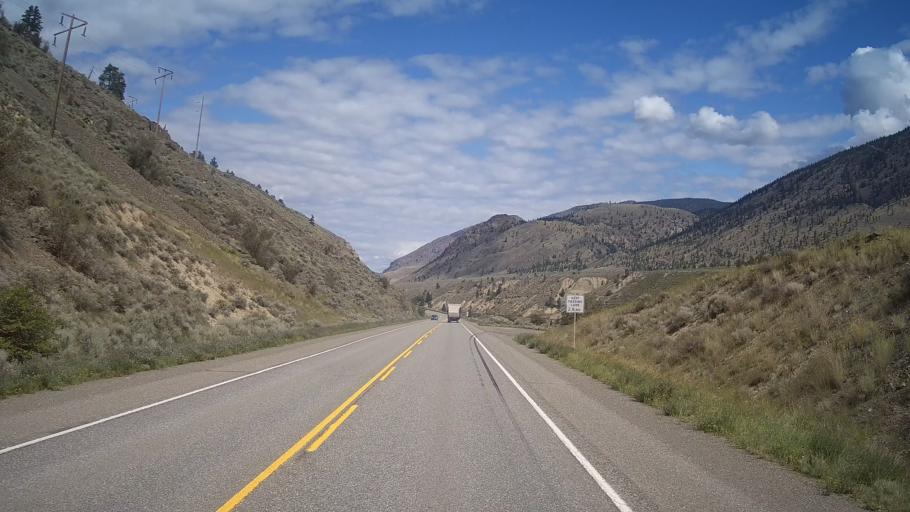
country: CA
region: British Columbia
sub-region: Thompson-Nicola Regional District
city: Ashcroft
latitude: 50.5300
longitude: -121.2857
